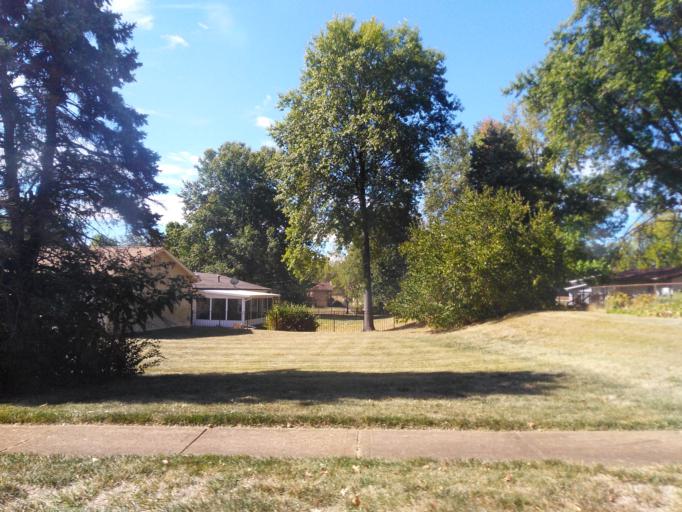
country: US
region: Missouri
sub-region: Saint Louis County
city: Concord
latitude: 38.5022
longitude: -90.3767
